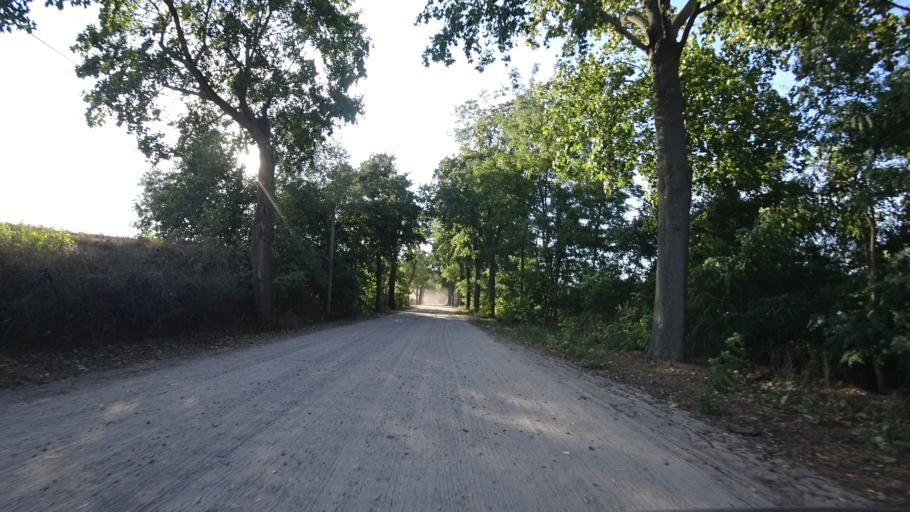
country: DE
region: Brandenburg
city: Stahnsdorf
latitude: 52.3449
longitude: 13.1756
